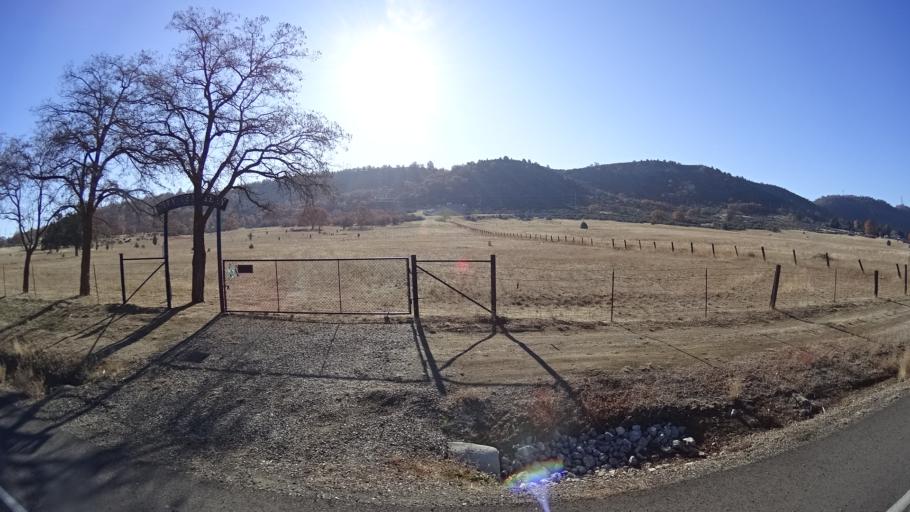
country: US
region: California
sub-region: Siskiyou County
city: Yreka
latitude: 41.7372
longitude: -122.6205
